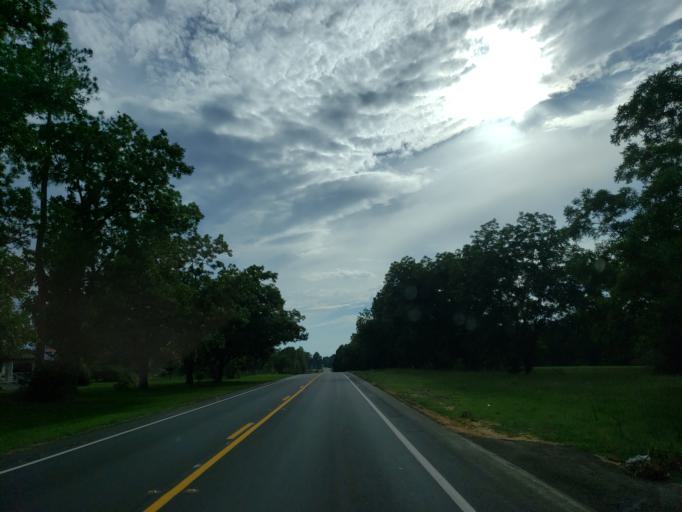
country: US
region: Georgia
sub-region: Irwin County
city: Ocilla
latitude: 31.5621
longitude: -83.3528
